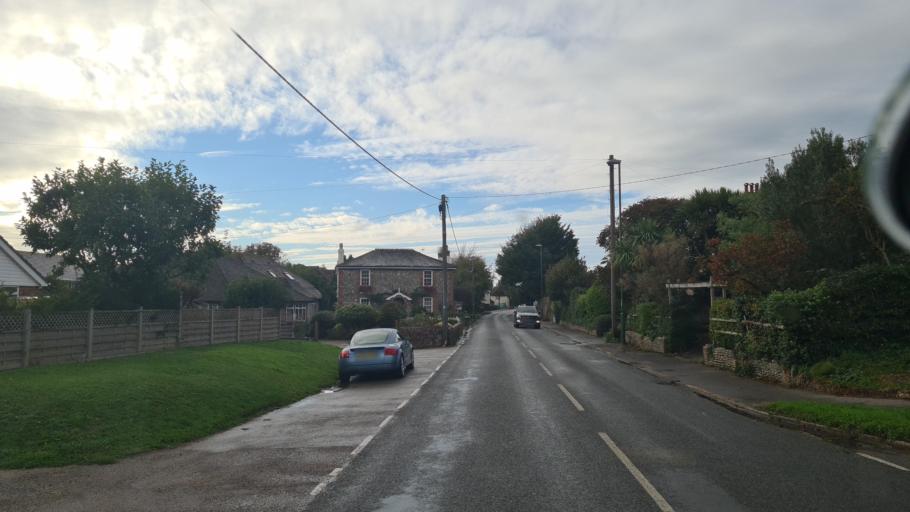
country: GB
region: England
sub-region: West Sussex
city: Walberton
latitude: 50.8176
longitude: -0.6027
